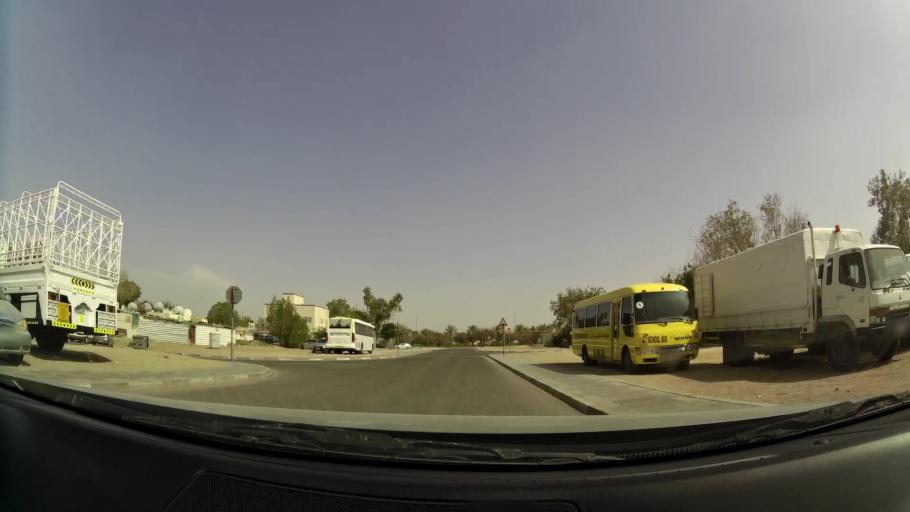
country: AE
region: Abu Dhabi
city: Al Ain
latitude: 24.2310
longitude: 55.6949
